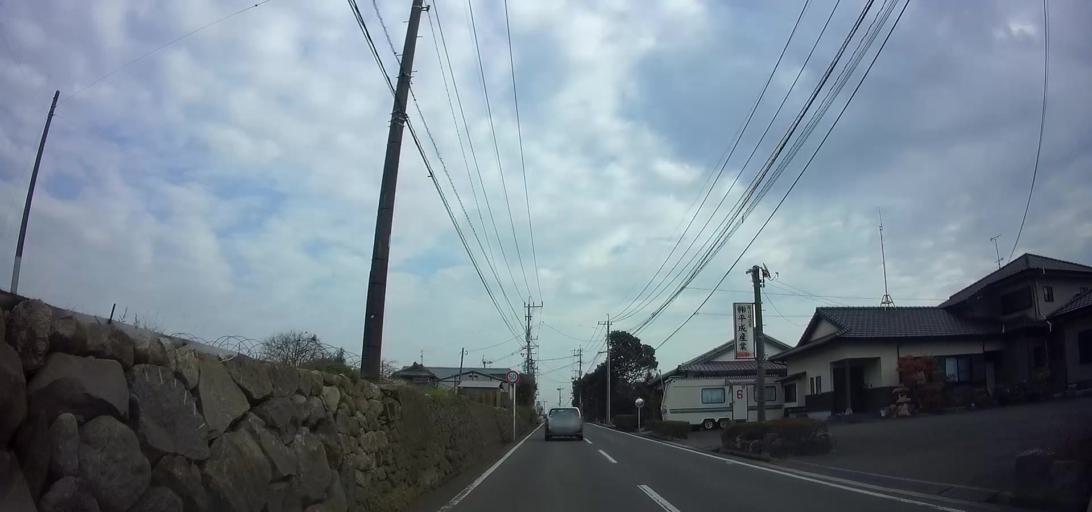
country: JP
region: Nagasaki
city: Shimabara
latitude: 32.6955
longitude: 130.3250
